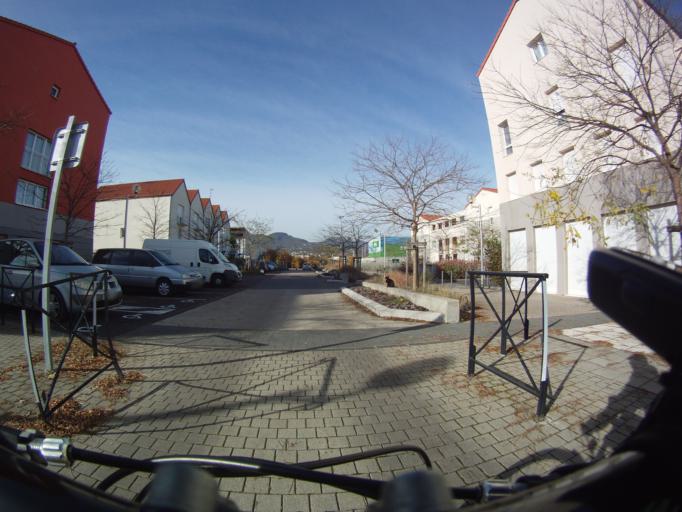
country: FR
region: Auvergne
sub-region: Departement du Puy-de-Dome
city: Aubiere
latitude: 45.7506
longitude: 3.1007
